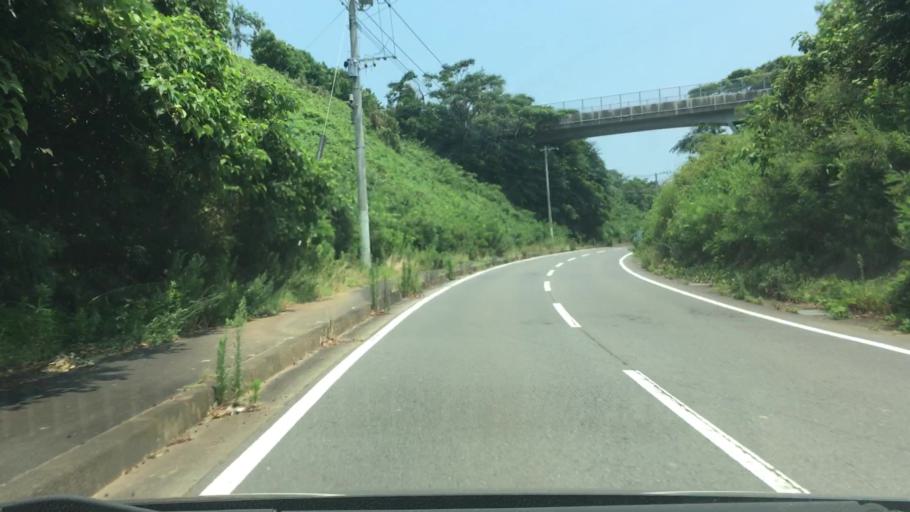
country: JP
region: Nagasaki
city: Sasebo
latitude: 33.0659
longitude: 129.6731
